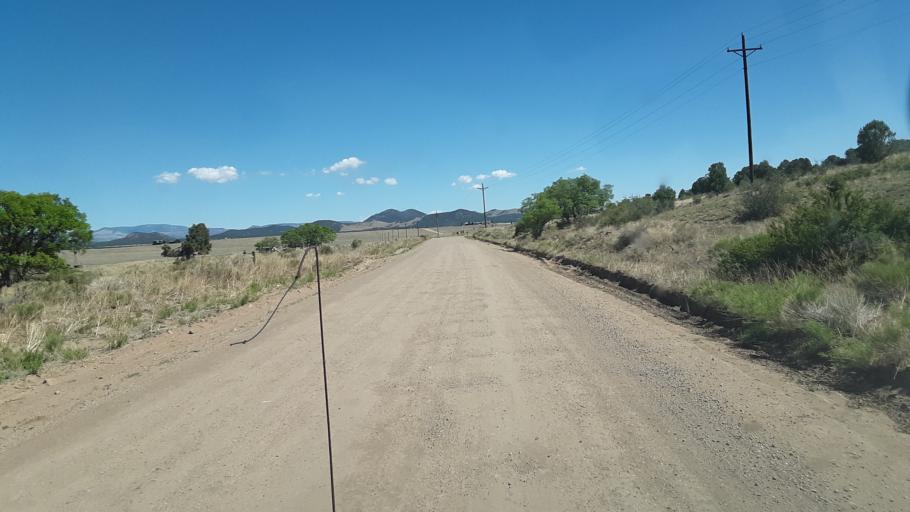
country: US
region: Colorado
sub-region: Custer County
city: Westcliffe
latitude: 38.2459
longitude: -105.5009
